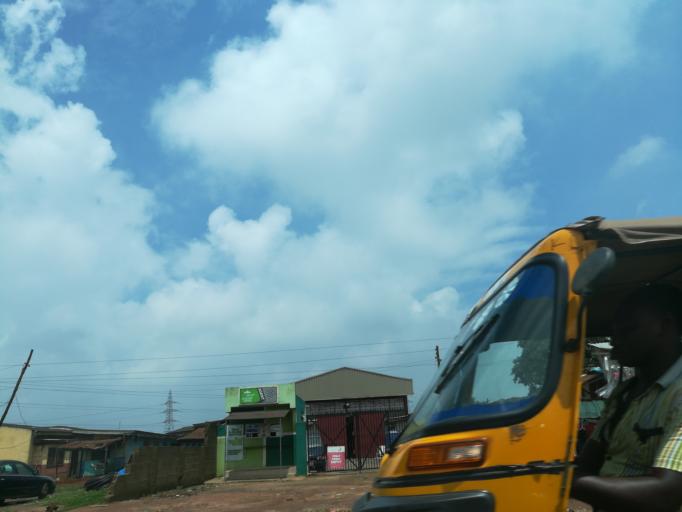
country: NG
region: Lagos
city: Ikorodu
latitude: 6.6789
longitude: 3.5117
